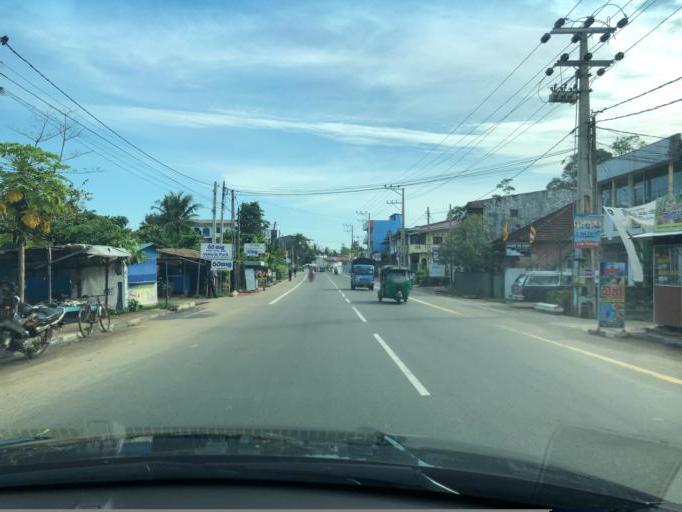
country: LK
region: Western
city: Kalutara
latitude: 6.5641
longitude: 79.9846
